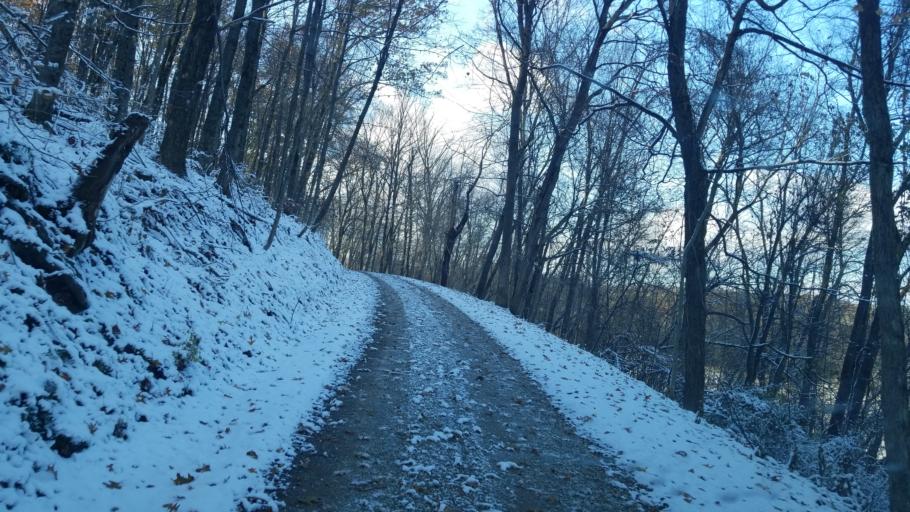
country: US
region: Ohio
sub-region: Licking County
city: Utica
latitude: 40.1622
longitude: -82.3948
